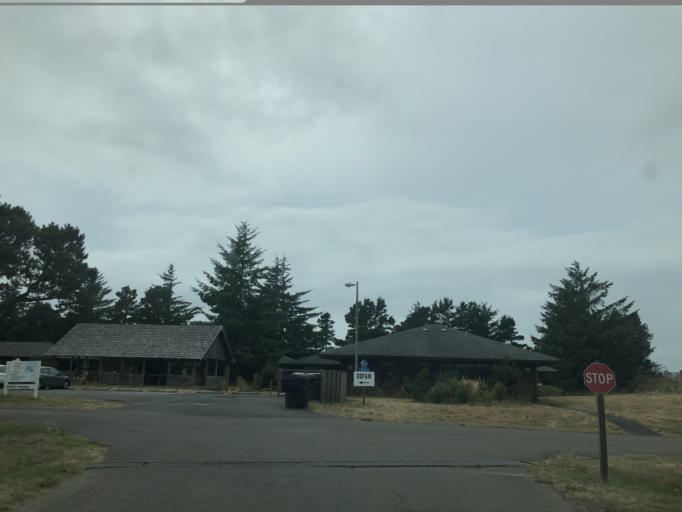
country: US
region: Oregon
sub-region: Lincoln County
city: Newport
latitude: 44.6208
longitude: -124.0455
